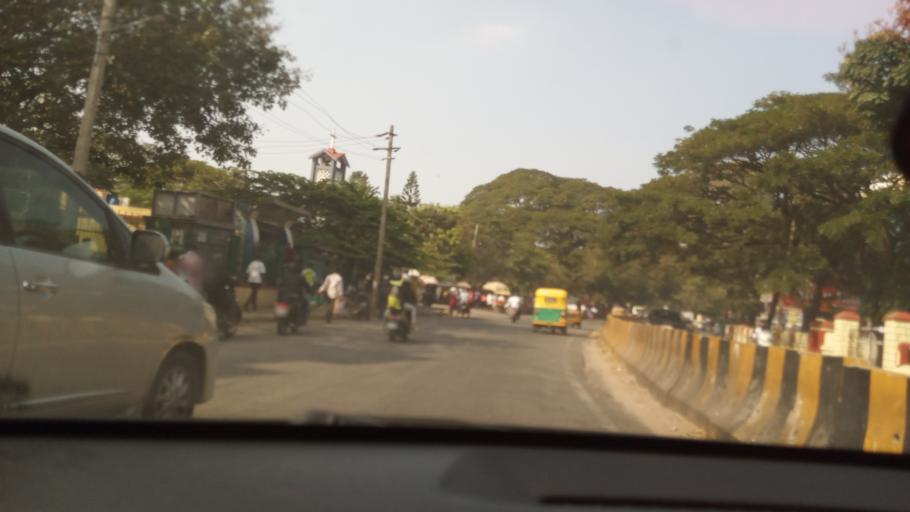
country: IN
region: Karnataka
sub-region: Mysore
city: Mysore
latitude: 12.3103
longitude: 76.6587
